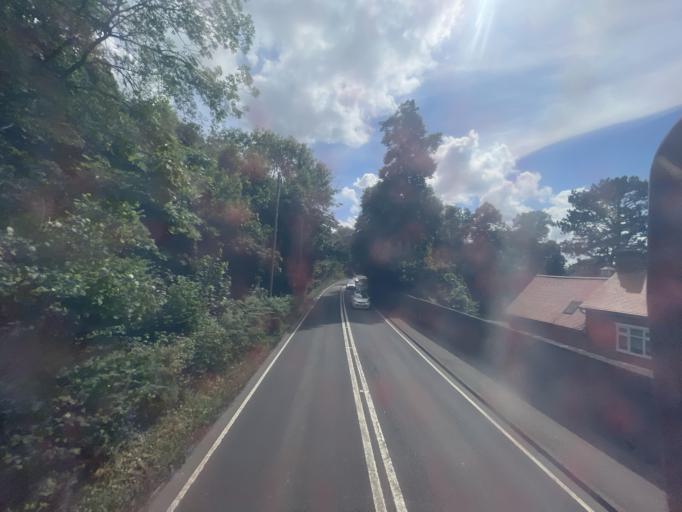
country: GB
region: England
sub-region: Kent
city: Biggin Hill
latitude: 51.3535
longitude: 0.0324
